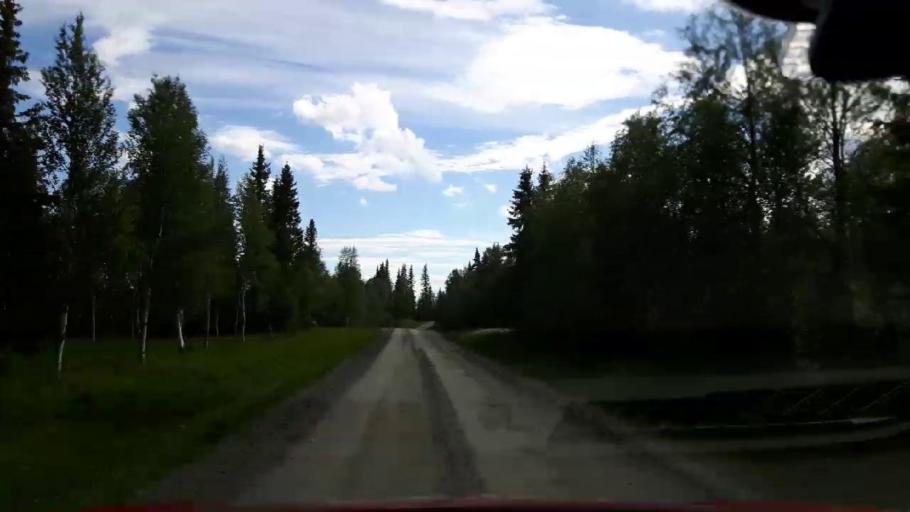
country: SE
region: Jaemtland
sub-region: Krokoms Kommun
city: Valla
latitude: 63.8581
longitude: 14.0978
